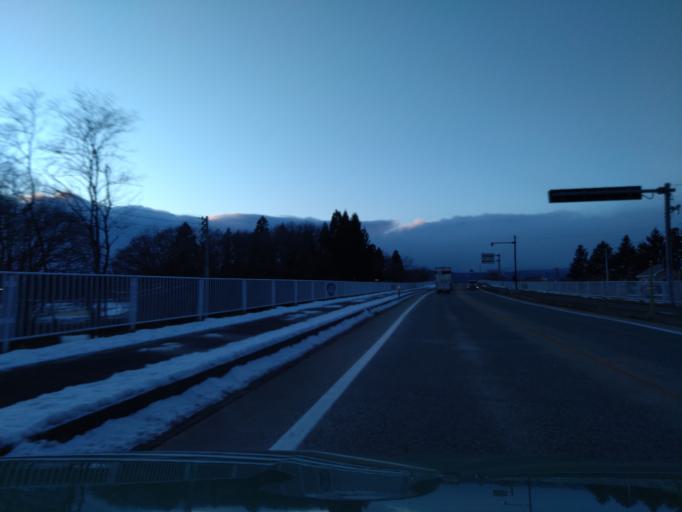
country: JP
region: Iwate
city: Shizukuishi
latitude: 39.6899
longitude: 140.9901
